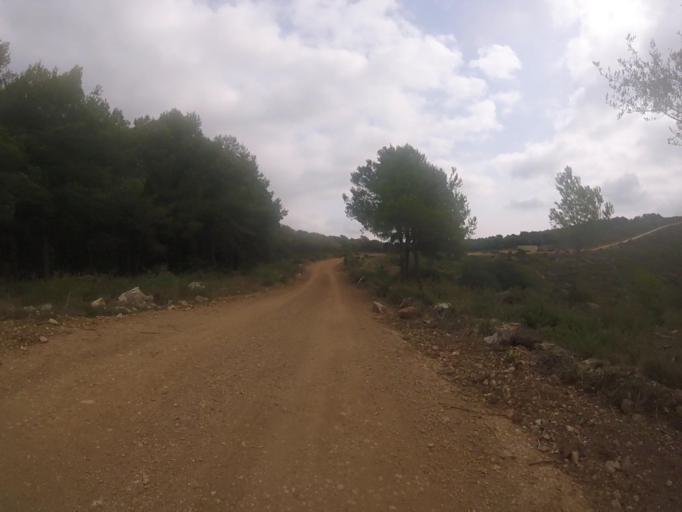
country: ES
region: Valencia
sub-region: Provincia de Castello
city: Santa Magdalena de Pulpis
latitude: 40.3463
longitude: 0.3237
